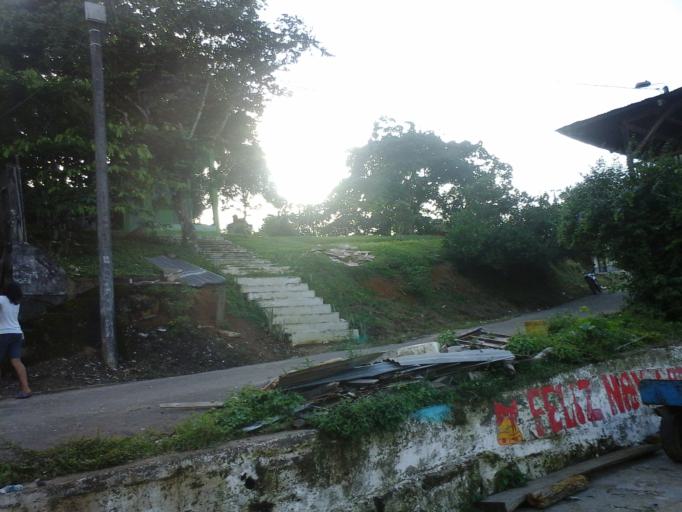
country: CO
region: Caqueta
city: El Doncello
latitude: 1.6126
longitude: -74.9940
